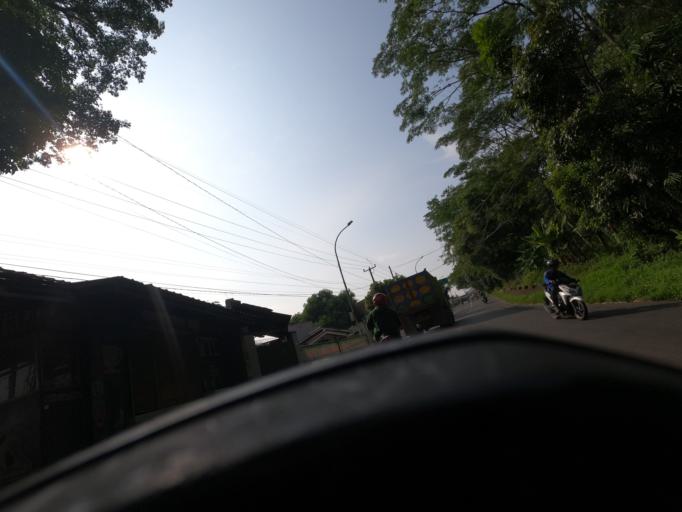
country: ID
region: West Java
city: Lembang
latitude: -6.6325
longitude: 107.7229
